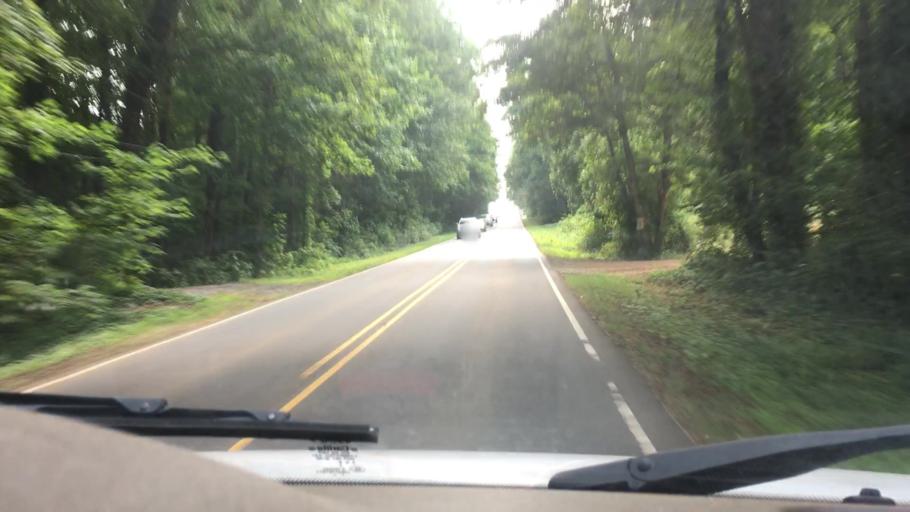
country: US
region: North Carolina
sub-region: Mecklenburg County
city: Huntersville
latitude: 35.4017
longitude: -80.9186
